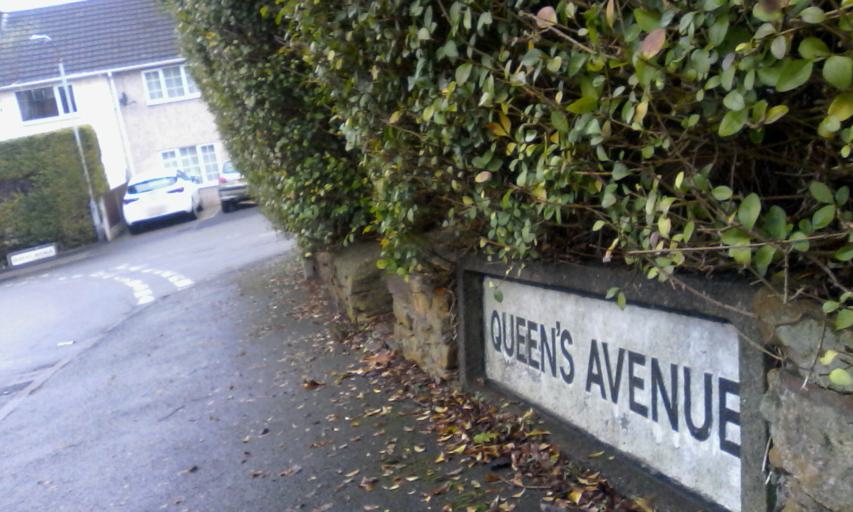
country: GB
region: England
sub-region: Nottinghamshire
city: Burton Joyce
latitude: 52.9770
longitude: -1.0852
